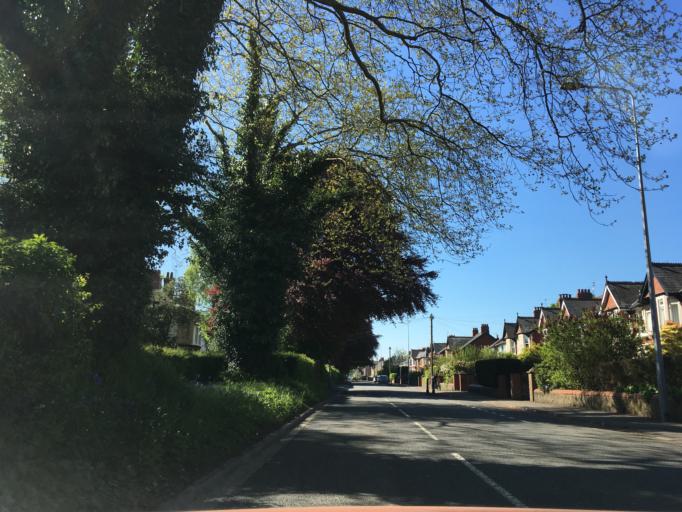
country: GB
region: Wales
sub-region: Cardiff
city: Radyr
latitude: 51.5170
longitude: -3.2263
